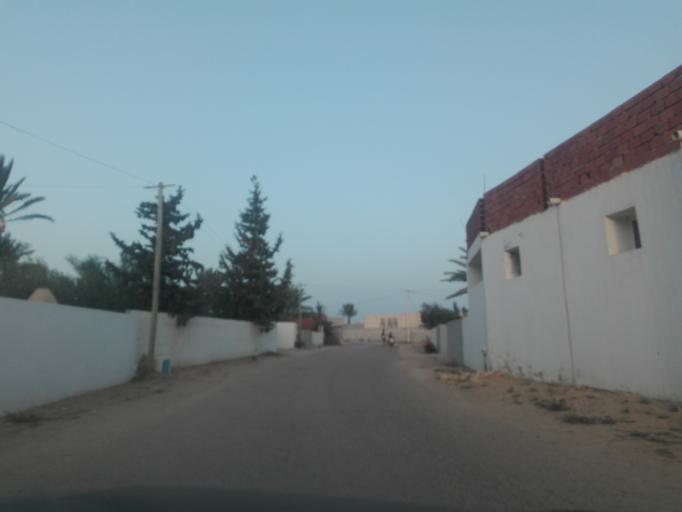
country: TN
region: Madanin
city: Houmt Souk
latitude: 33.7307
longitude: 10.7509
